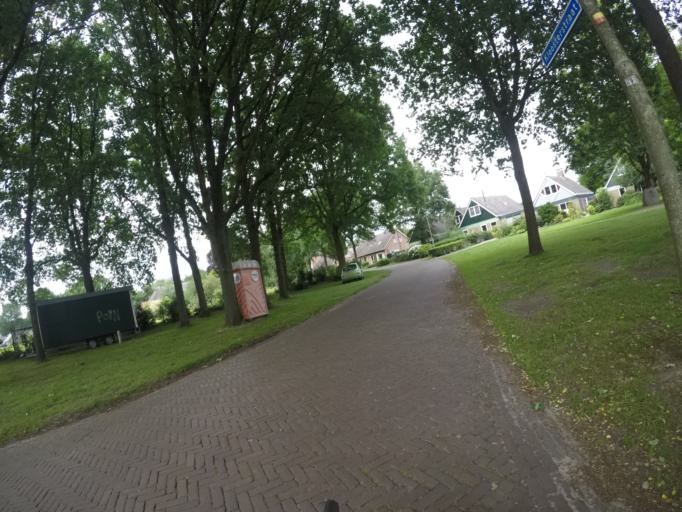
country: NL
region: Drenthe
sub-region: Gemeente Westerveld
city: Dwingeloo
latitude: 52.8537
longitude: 6.3173
